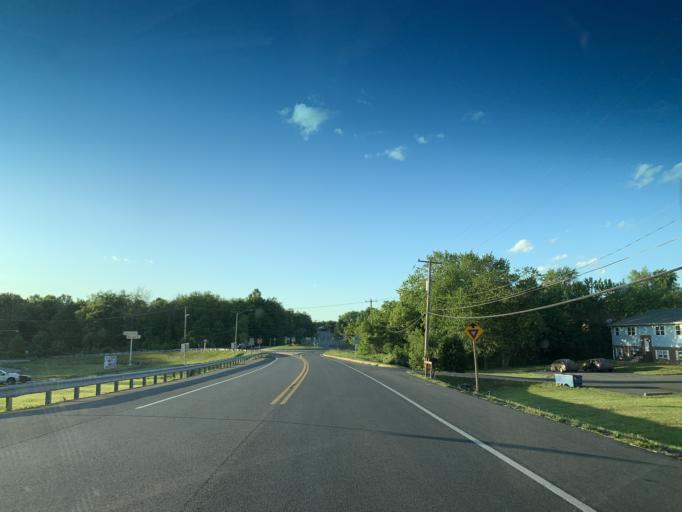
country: US
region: Maryland
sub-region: Cecil County
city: Elkton
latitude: 39.6624
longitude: -75.8551
